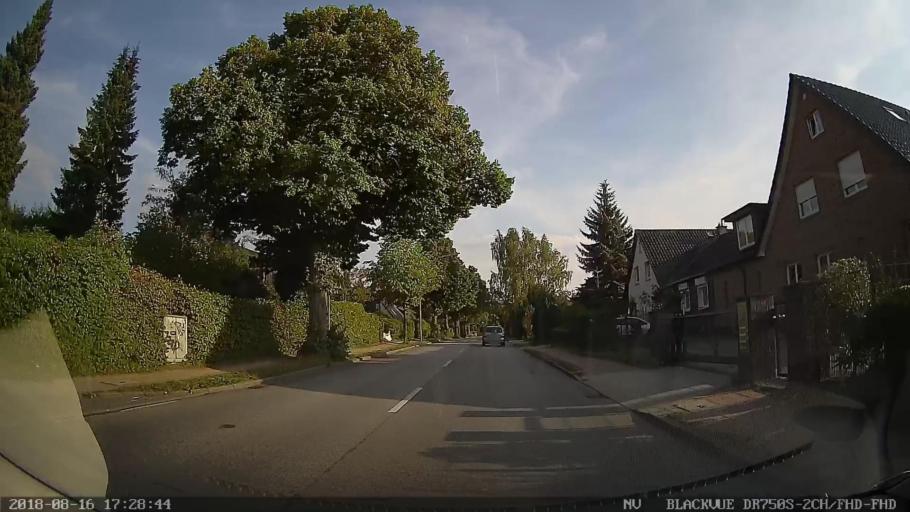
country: DE
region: Hamburg
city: Eidelstedt
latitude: 53.5830
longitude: 9.8664
